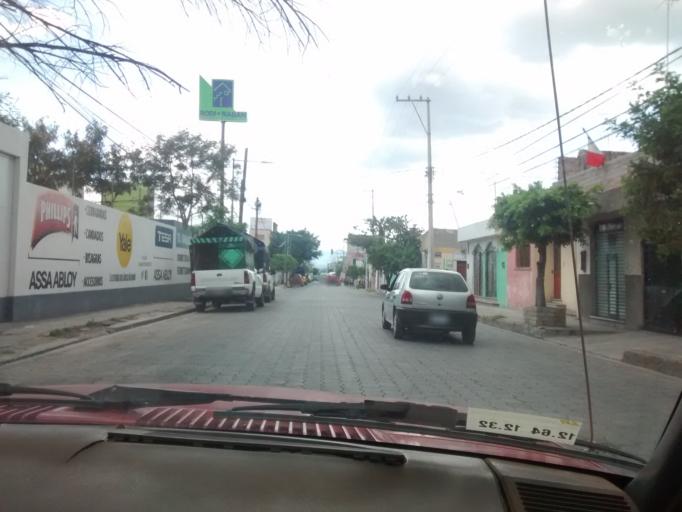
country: MX
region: Puebla
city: Tehuacan
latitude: 18.4617
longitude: -97.3849
